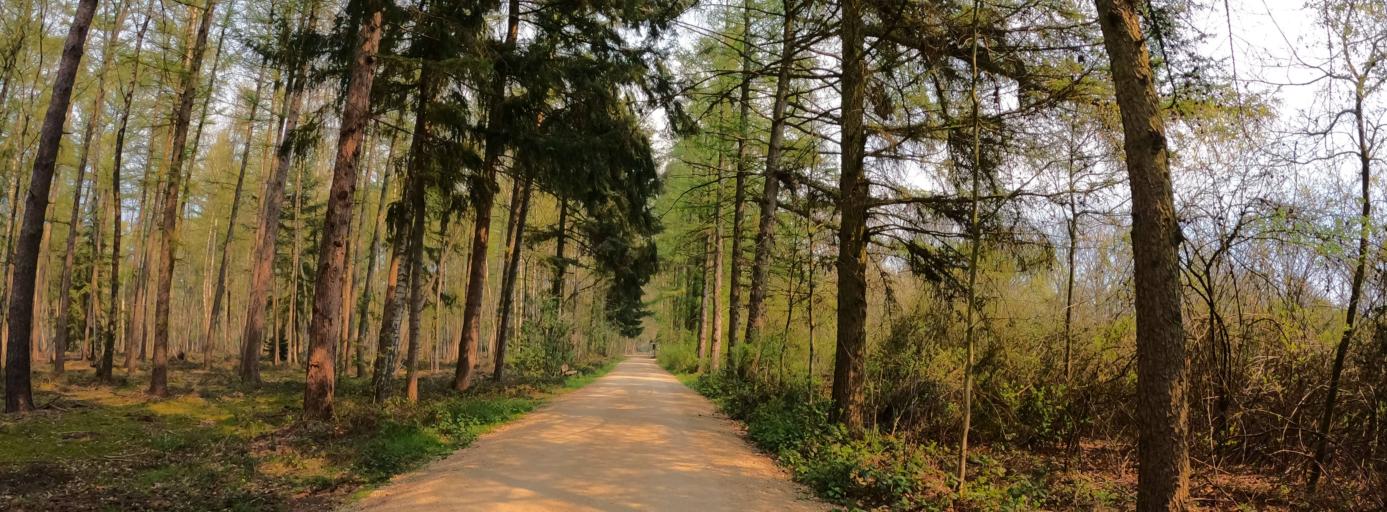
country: BE
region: Flanders
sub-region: Provincie Antwerpen
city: Brasschaat
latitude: 51.3107
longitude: 4.5166
